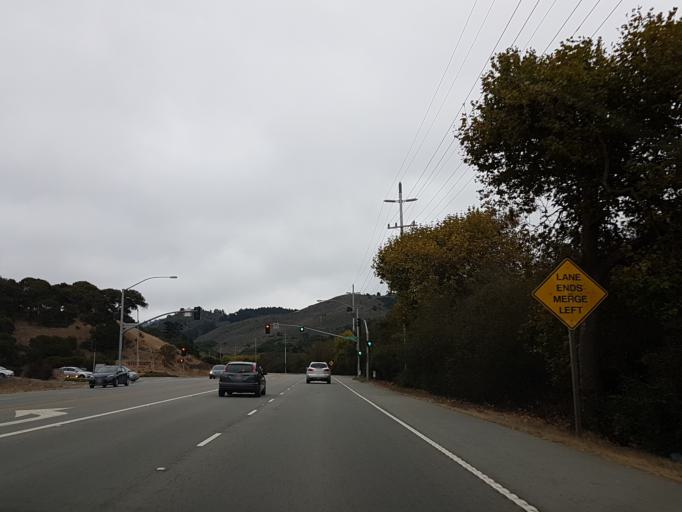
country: US
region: California
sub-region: Monterey County
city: Del Rey Oaks
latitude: 36.5786
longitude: -121.8258
